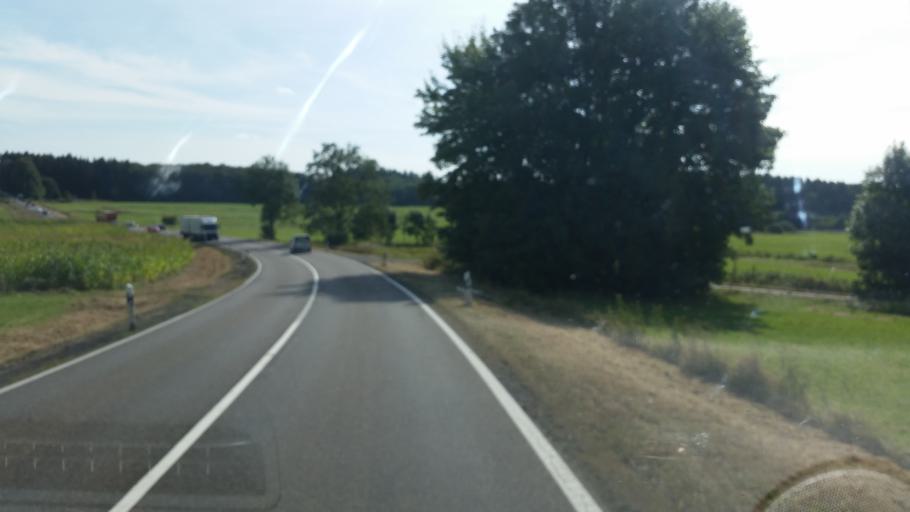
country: DE
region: Rheinland-Pfalz
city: Kaden
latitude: 50.5481
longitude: 7.8835
